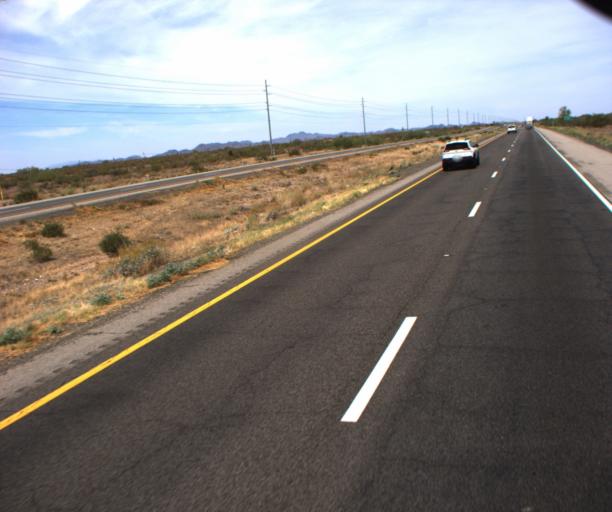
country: US
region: Arizona
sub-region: Maricopa County
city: Sun City West
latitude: 33.7933
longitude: -112.5481
